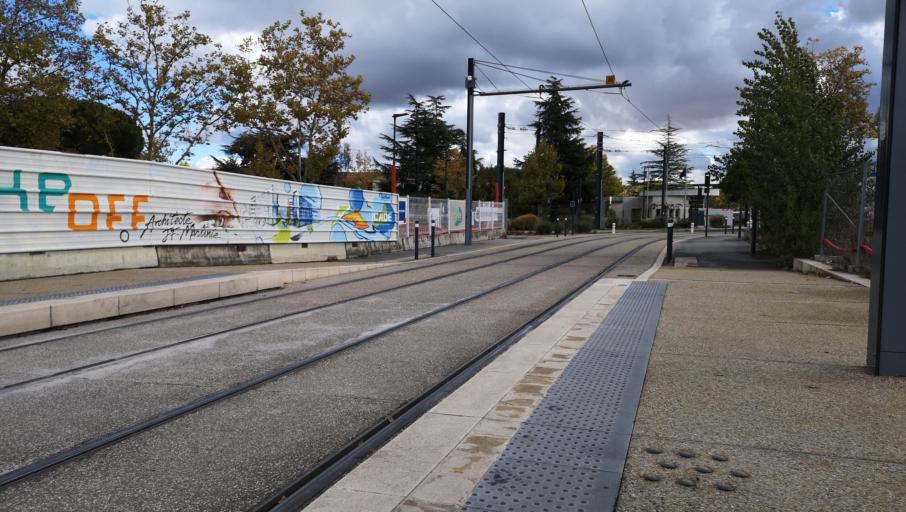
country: FR
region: Midi-Pyrenees
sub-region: Departement de la Haute-Garonne
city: Blagnac
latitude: 43.6288
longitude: 1.3794
